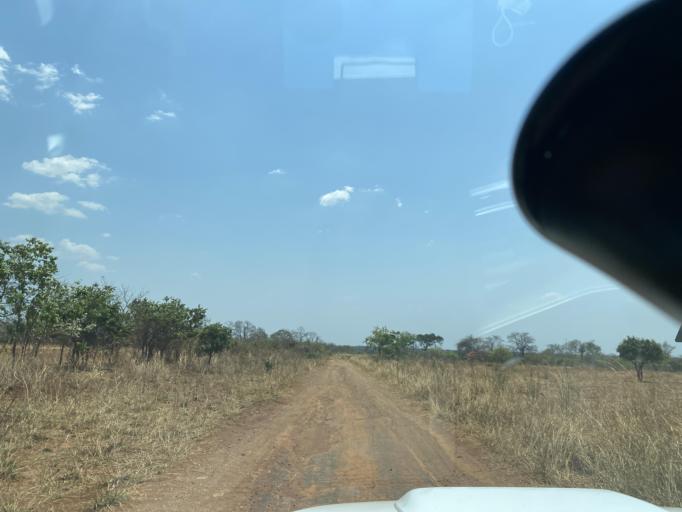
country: ZM
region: Lusaka
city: Lusaka
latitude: -15.5062
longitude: 28.0172
